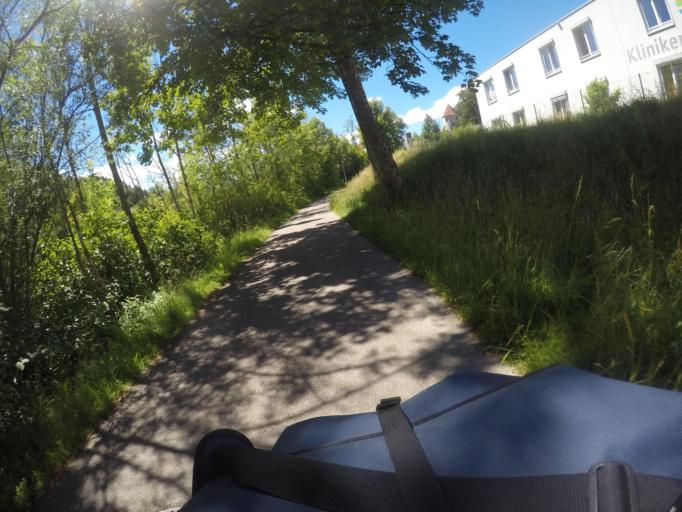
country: DE
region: Bavaria
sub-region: Swabia
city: Fuessen
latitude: 47.5659
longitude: 10.7048
